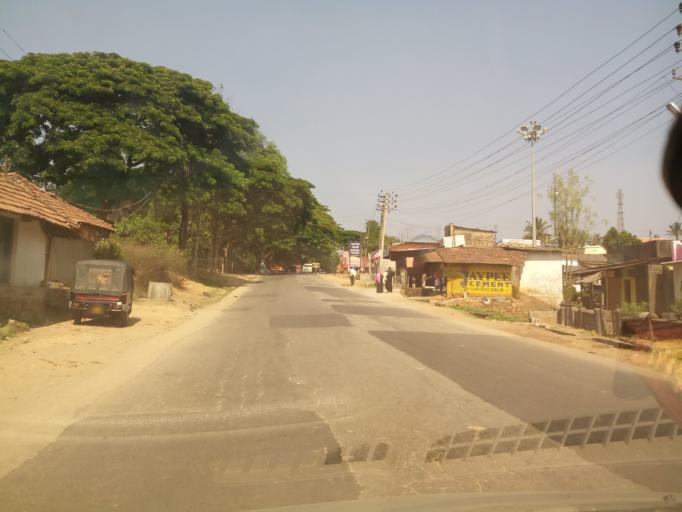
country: IN
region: Karnataka
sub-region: Hassan
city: Sakleshpur
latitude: 12.9483
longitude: 75.8027
